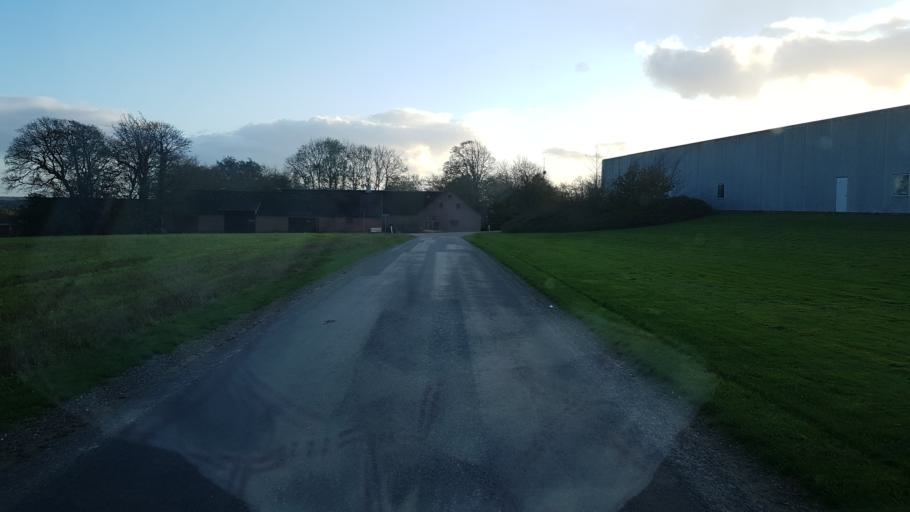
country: DK
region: South Denmark
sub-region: Vejen Kommune
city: Holsted
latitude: 55.4530
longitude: 8.9422
